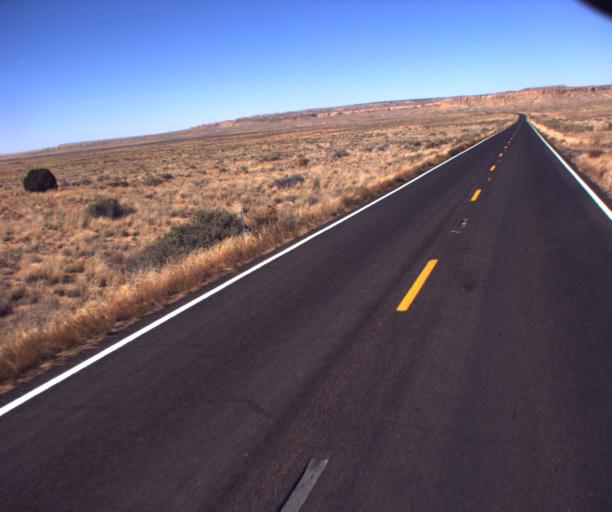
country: US
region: Arizona
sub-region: Navajo County
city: First Mesa
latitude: 35.9669
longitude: -110.6918
